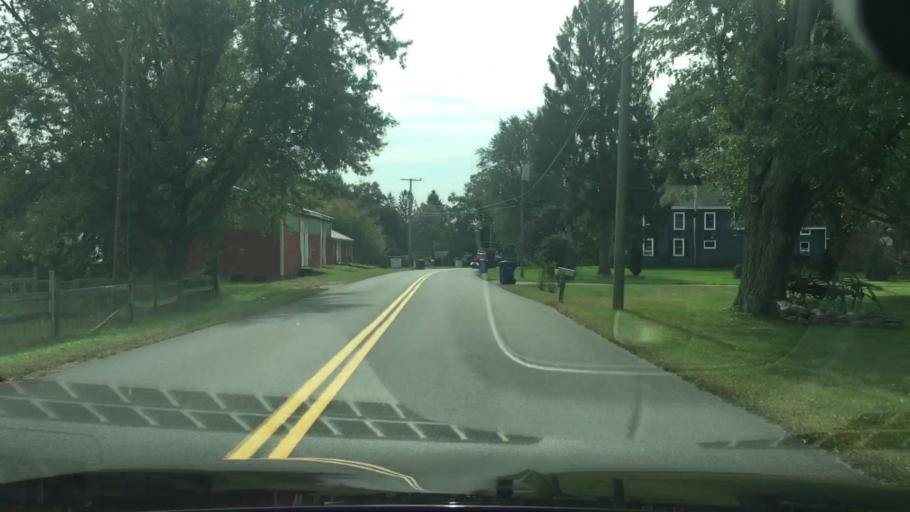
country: US
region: Connecticut
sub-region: Tolland County
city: Ellington
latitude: 41.9386
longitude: -72.4787
